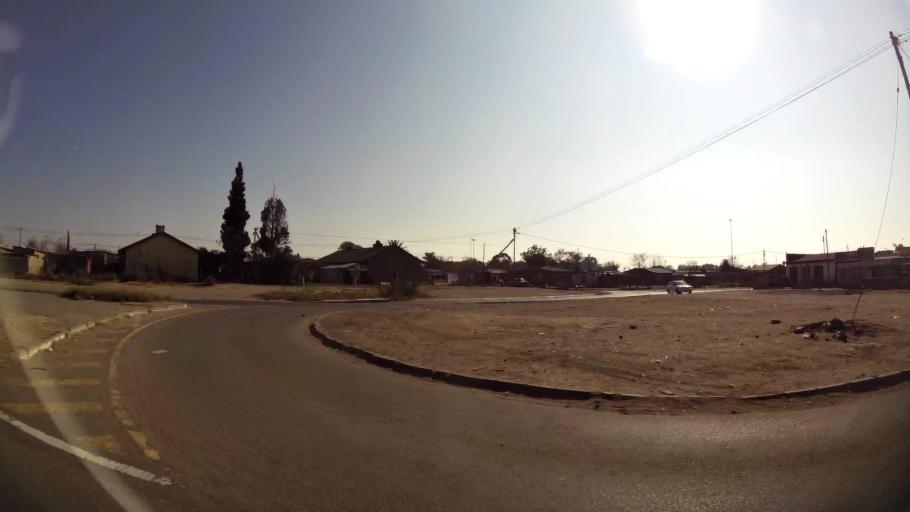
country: ZA
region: Orange Free State
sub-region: Mangaung Metropolitan Municipality
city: Bloemfontein
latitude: -29.1341
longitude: 26.2319
